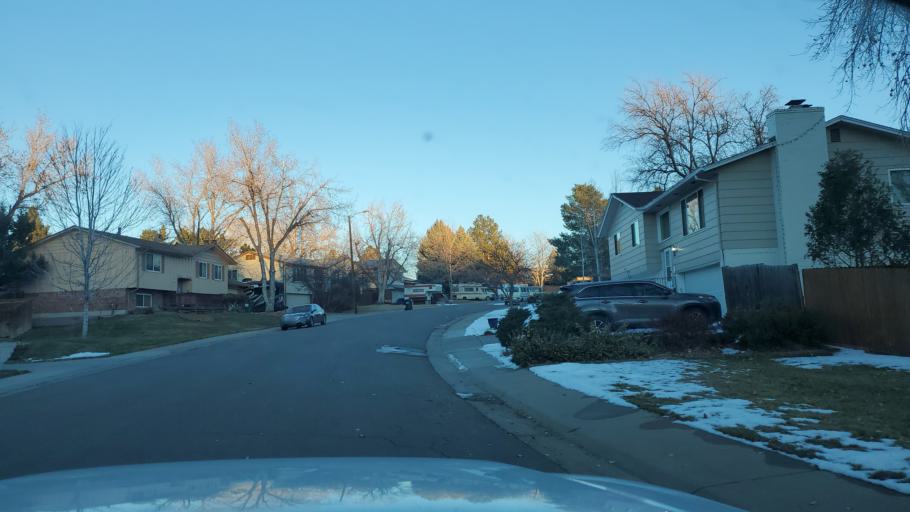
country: US
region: Colorado
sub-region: Arapahoe County
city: Castlewood
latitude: 39.5898
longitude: -104.9028
